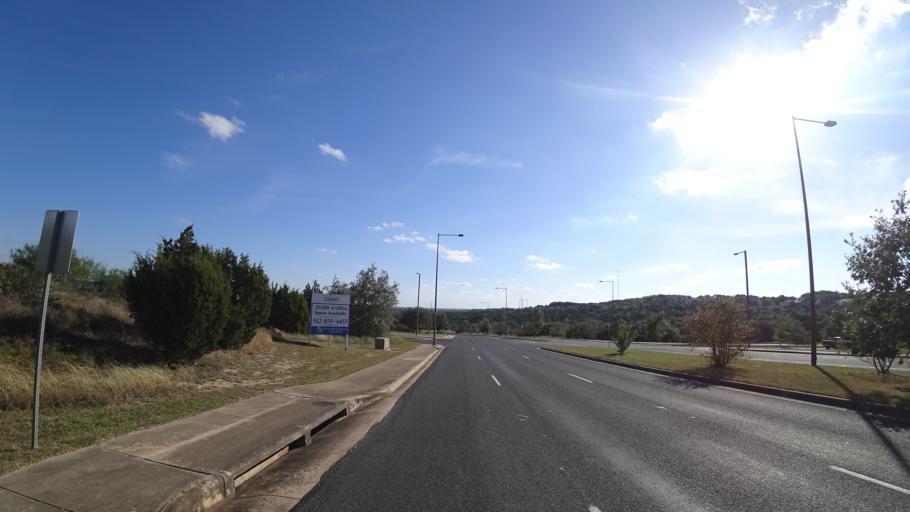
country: US
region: Texas
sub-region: Travis County
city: Barton Creek
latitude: 30.2504
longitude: -97.8663
